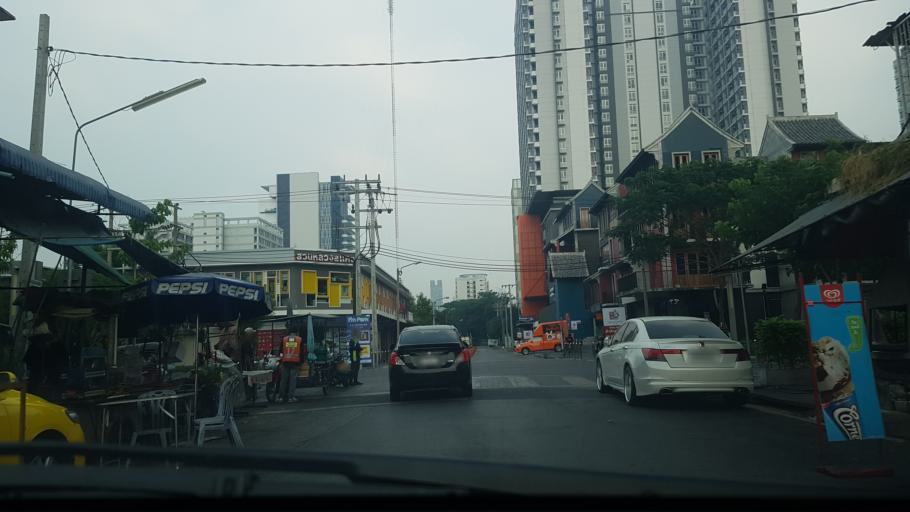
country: TH
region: Bangkok
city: Pathum Wan
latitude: 13.7422
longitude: 100.5238
